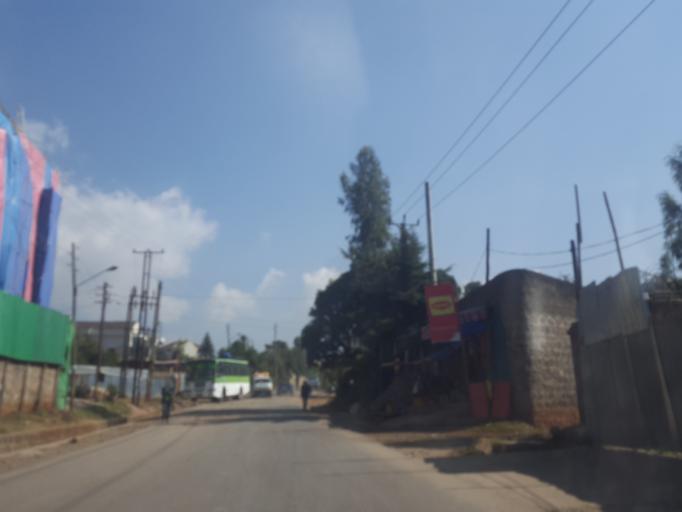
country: ET
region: Adis Abeba
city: Addis Ababa
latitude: 9.0514
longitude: 38.7287
